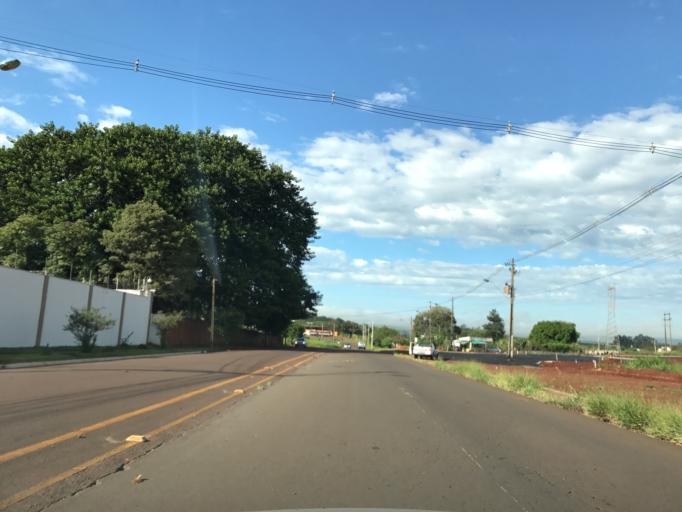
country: BR
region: Parana
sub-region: Maringa
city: Maringa
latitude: -23.4552
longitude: -51.9530
